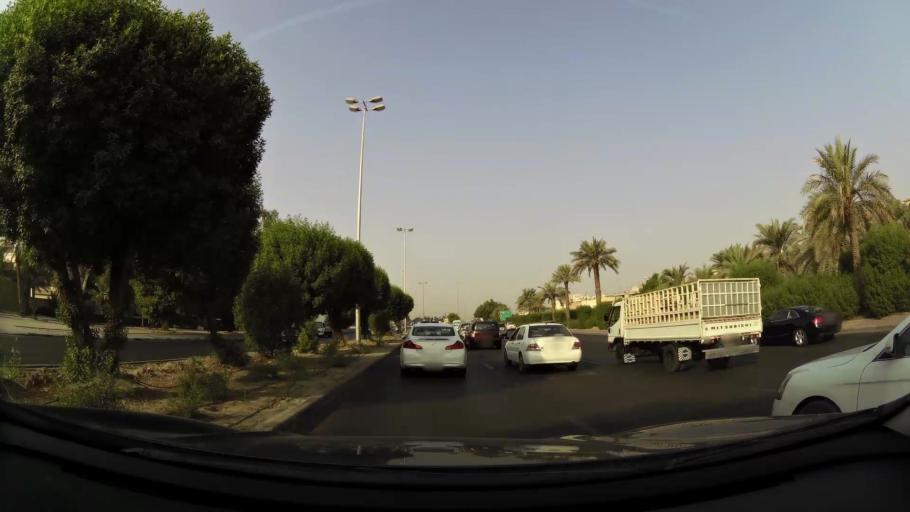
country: KW
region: Al Asimah
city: Ash Shamiyah
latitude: 29.3191
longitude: 47.9792
